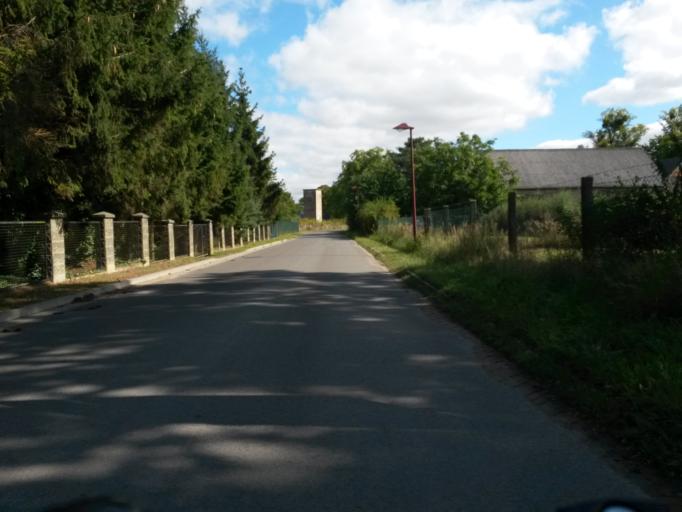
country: DE
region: Brandenburg
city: Templin
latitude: 53.2032
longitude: 13.5572
